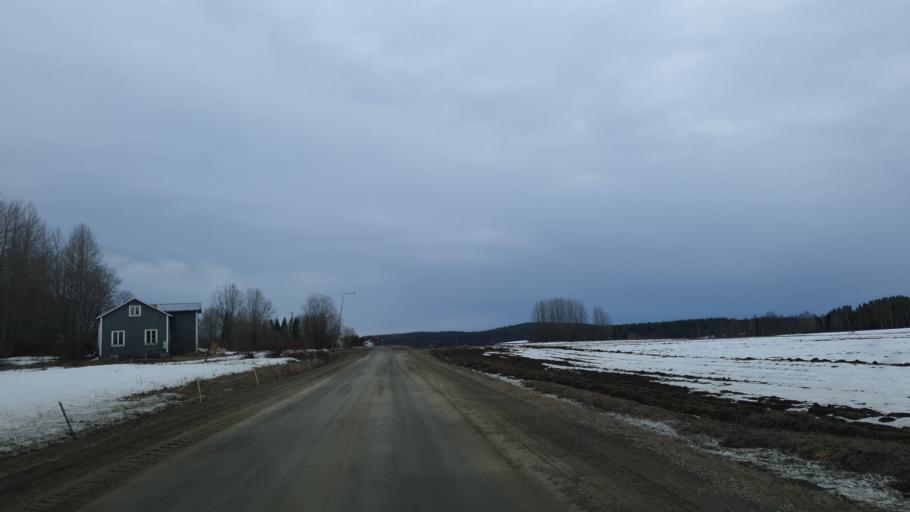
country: SE
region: Vaesterbotten
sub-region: Skelleftea Kommun
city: Burea
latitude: 64.3300
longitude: 21.1346
